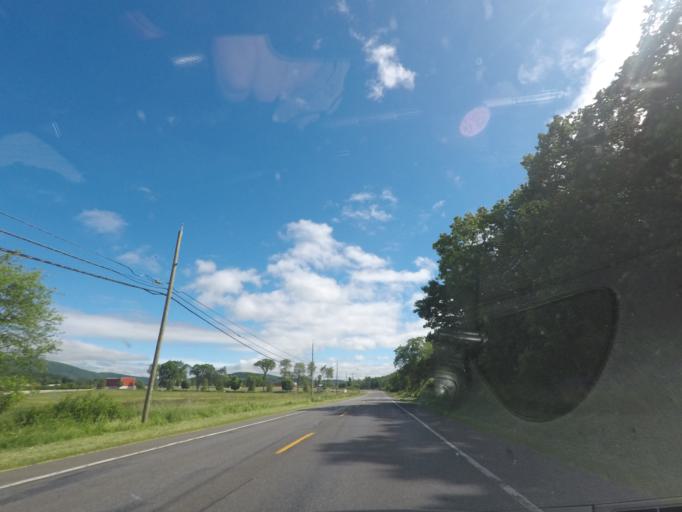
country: US
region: New York
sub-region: Dutchess County
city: Pine Plains
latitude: 42.0921
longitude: -73.5434
